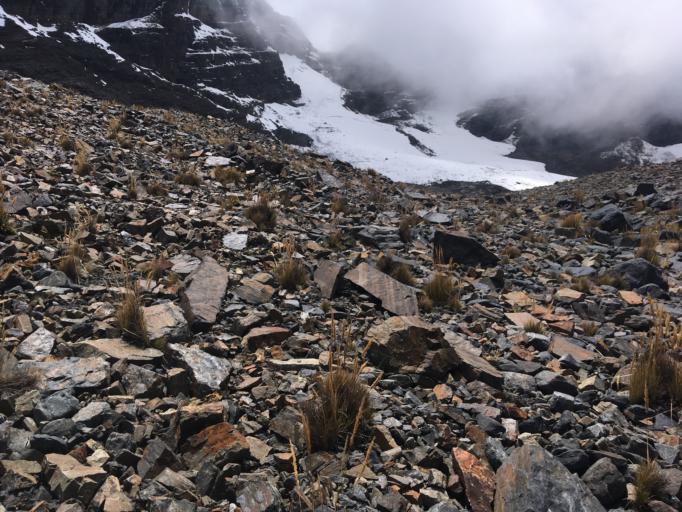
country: BO
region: La Paz
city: La Paz
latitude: -16.3979
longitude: -67.9477
